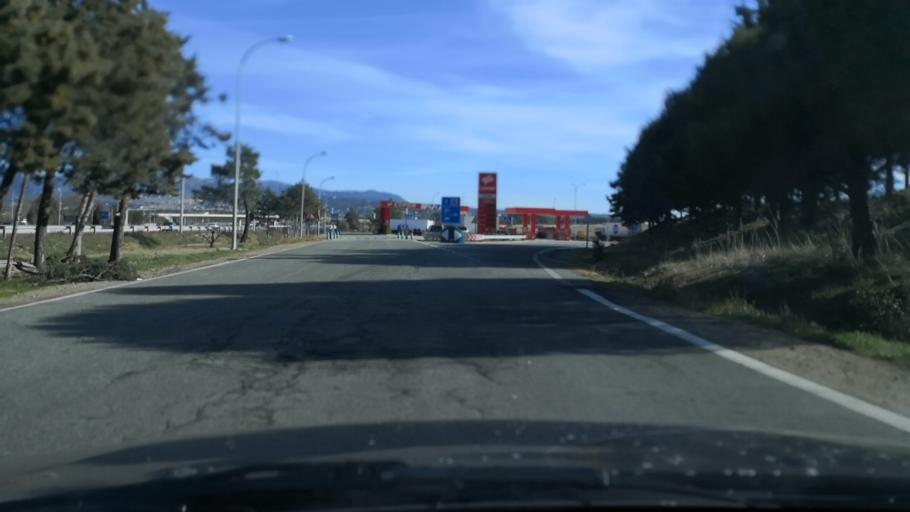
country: ES
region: Madrid
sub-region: Provincia de Madrid
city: Alpedrete
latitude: 40.6429
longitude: -4.0408
